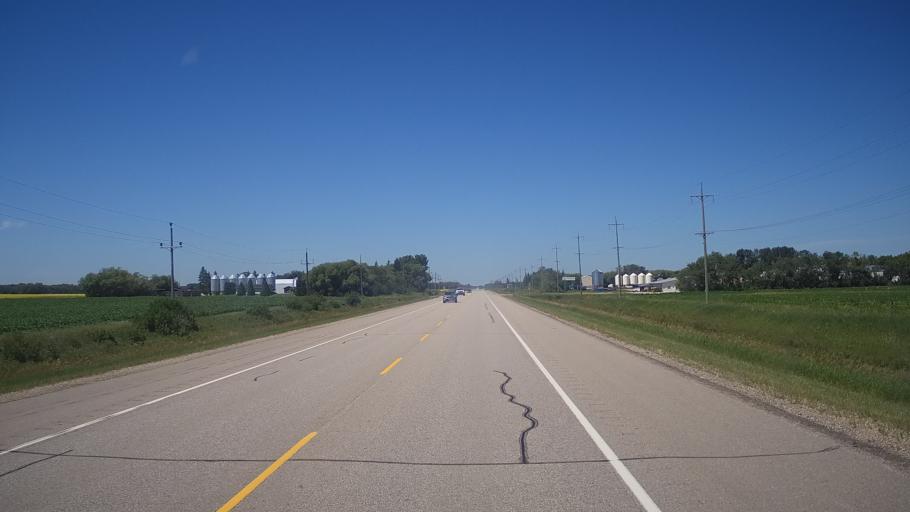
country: CA
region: Manitoba
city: Neepawa
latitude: 50.2252
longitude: -99.3135
